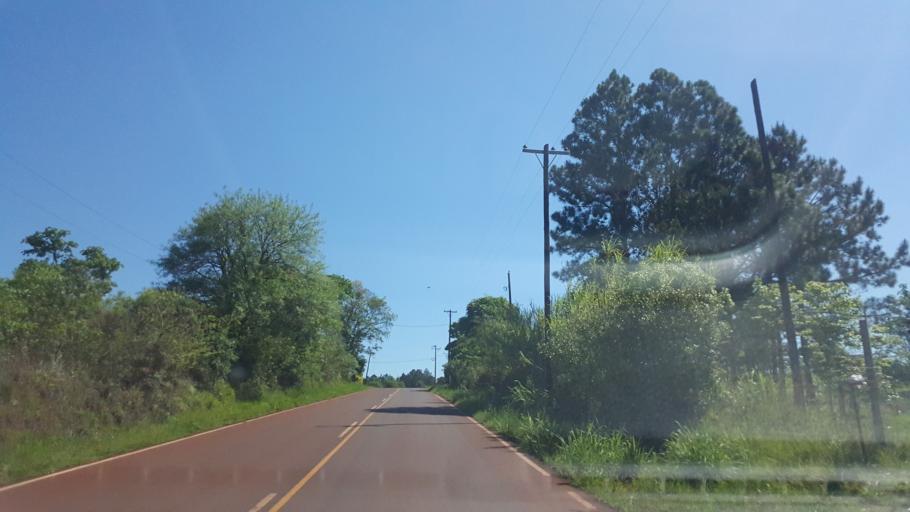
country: AR
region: Misiones
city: Garupa
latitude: -27.5053
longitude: -55.8549
